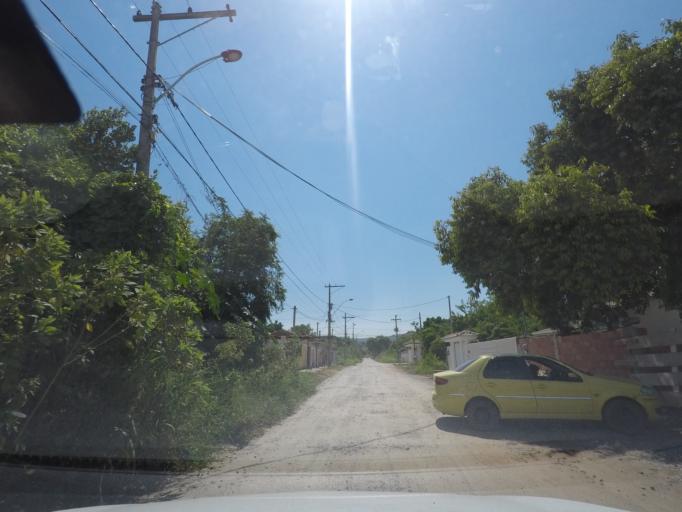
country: BR
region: Rio de Janeiro
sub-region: Marica
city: Marica
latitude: -22.9519
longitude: -42.9588
